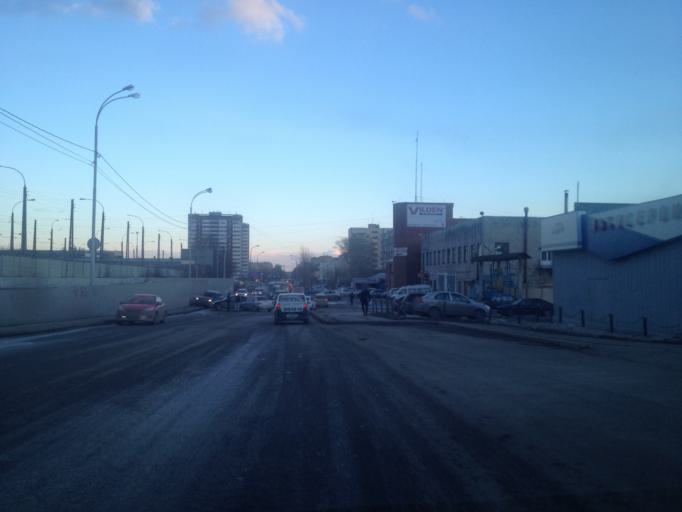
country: RU
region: Sverdlovsk
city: Sovkhoznyy
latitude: 56.8121
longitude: 60.5410
